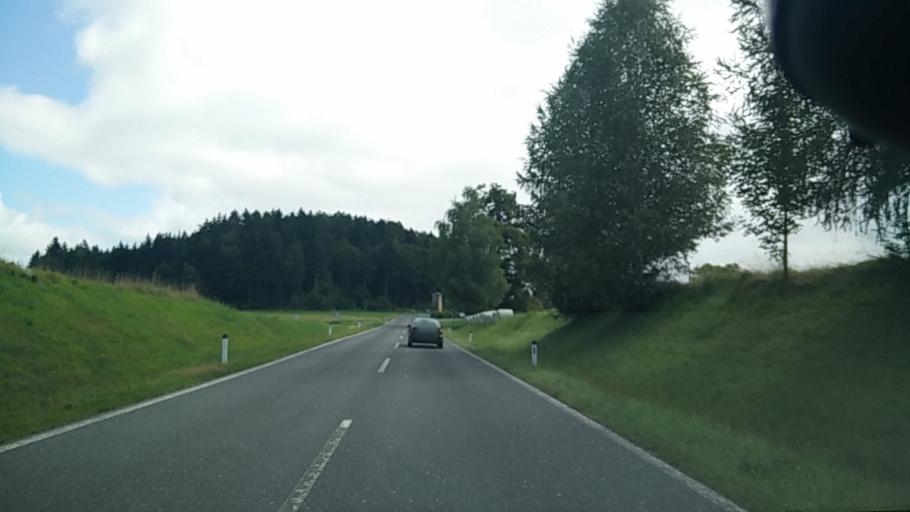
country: AT
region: Carinthia
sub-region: Politischer Bezirk Villach Land
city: Wernberg
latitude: 46.5578
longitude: 13.9398
